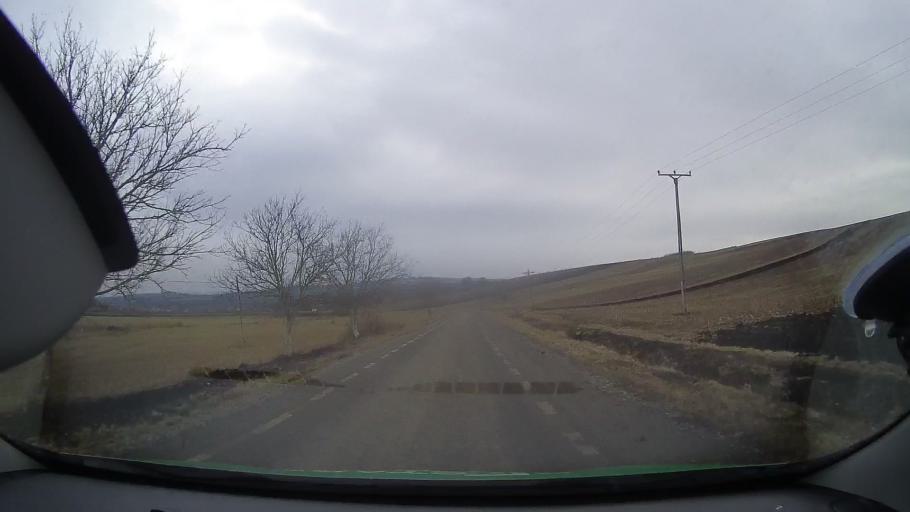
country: RO
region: Mures
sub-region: Comuna Bichis
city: Bichis
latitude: 46.3877
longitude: 24.0821
